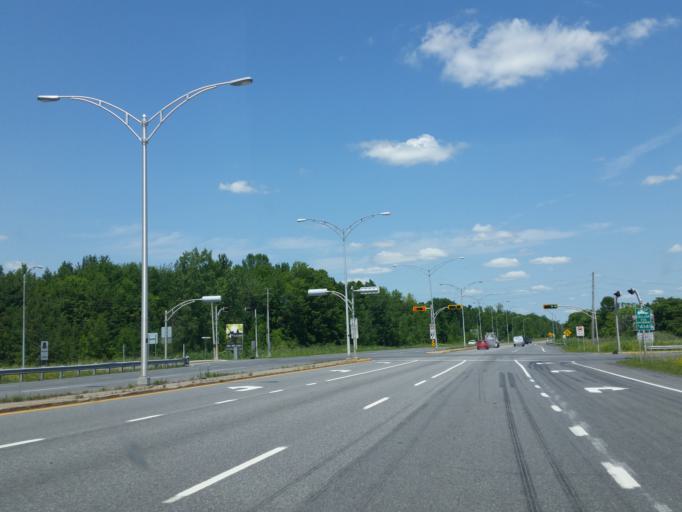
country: CA
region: Quebec
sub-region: Monteregie
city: Carignan
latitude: 45.4113
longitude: -73.3151
